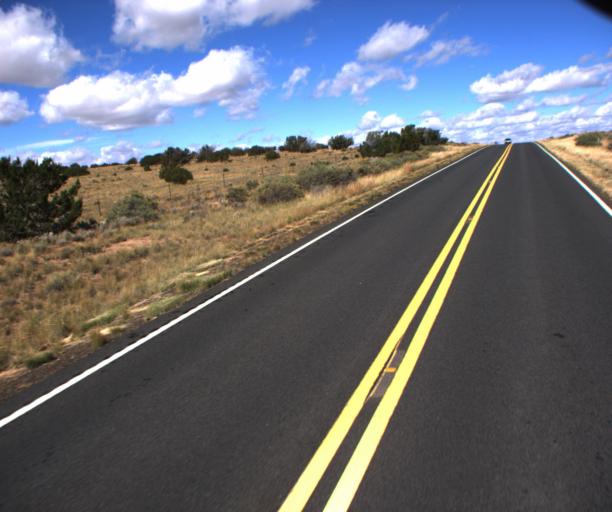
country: US
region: Arizona
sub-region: Apache County
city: Houck
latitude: 35.0205
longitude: -109.2418
